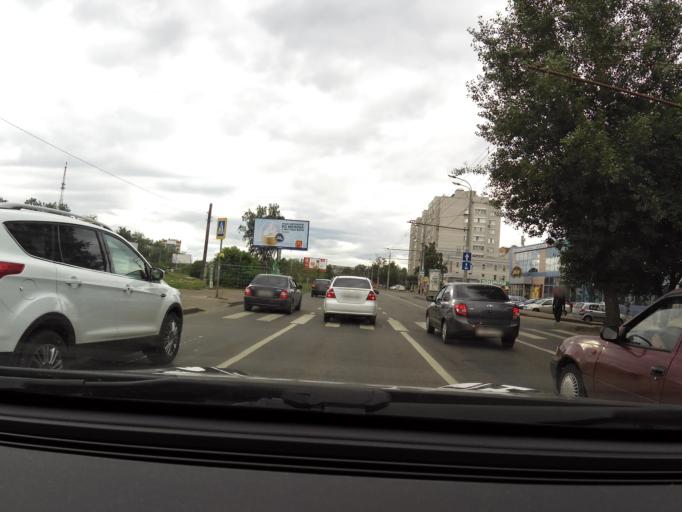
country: RU
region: Tatarstan
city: Staroye Arakchino
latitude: 55.8234
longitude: 49.0467
